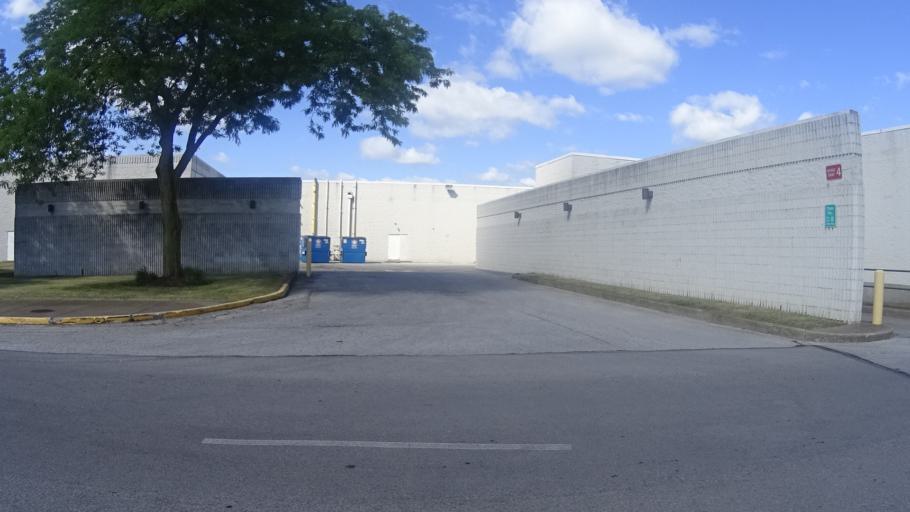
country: US
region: Ohio
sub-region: Erie County
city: Sandusky
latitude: 41.4179
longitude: -82.6671
